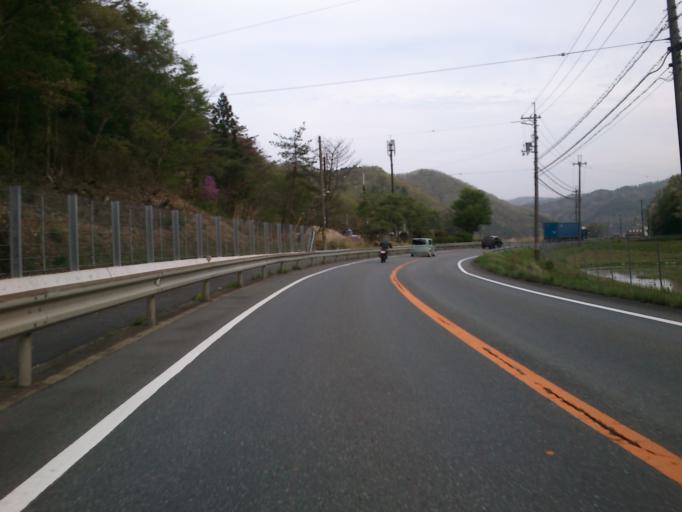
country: JP
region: Hyogo
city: Sasayama
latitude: 35.1316
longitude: 135.3334
